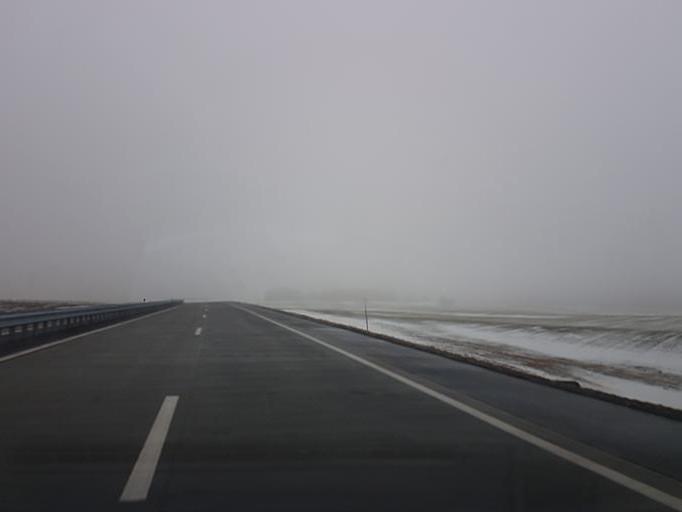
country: BY
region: Minsk
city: Atolina
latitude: 53.7517
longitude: 27.4120
